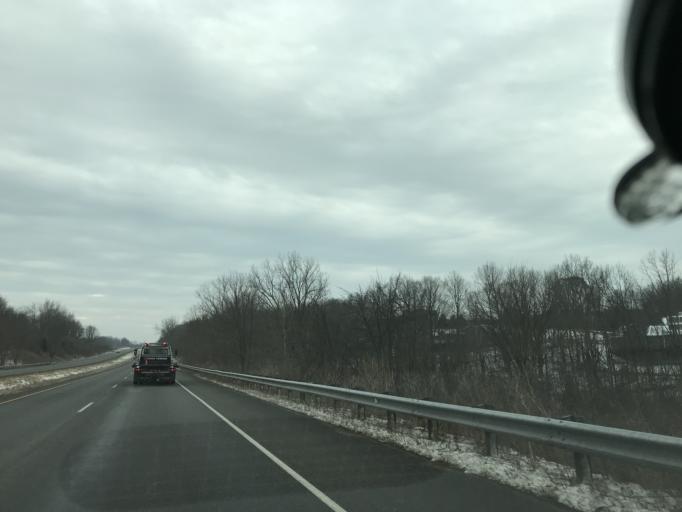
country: US
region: Michigan
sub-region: Kent County
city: Rockford
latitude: 43.1024
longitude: -85.5505
